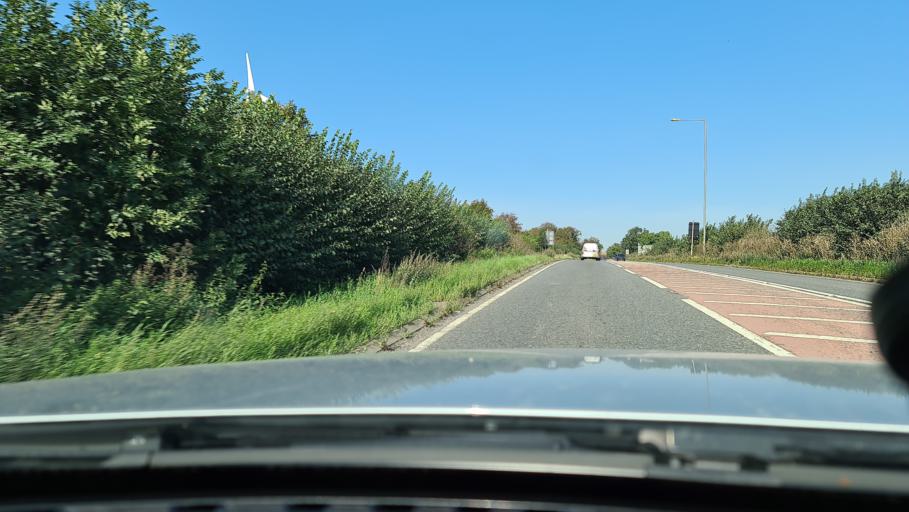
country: GB
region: England
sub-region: Leicestershire
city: Lutterworth
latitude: 52.3869
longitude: -1.1942
